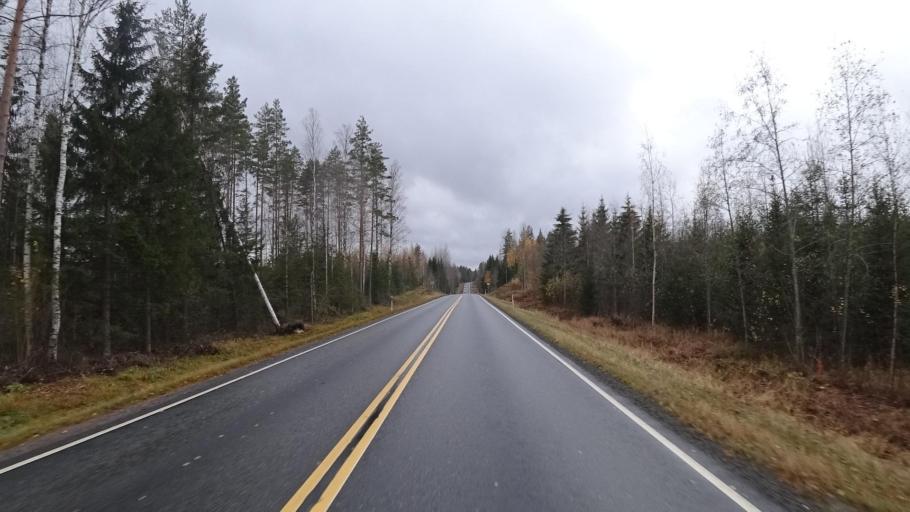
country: FI
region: Southern Savonia
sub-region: Mikkeli
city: Kangasniemi
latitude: 62.1714
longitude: 26.8556
